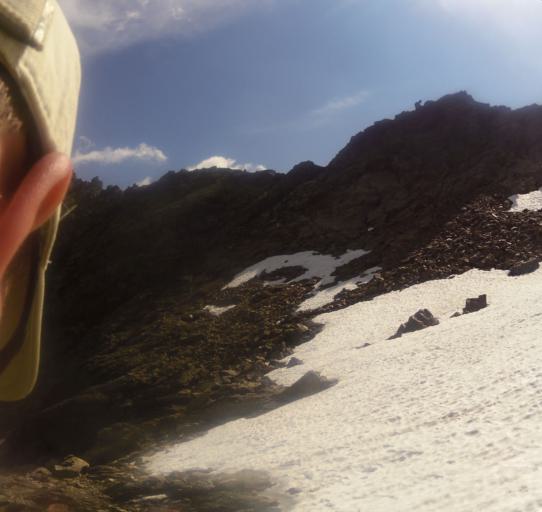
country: AT
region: Tyrol
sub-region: Politischer Bezirk Innsbruck Land
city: Gschnitz
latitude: 46.9908
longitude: 11.2442
